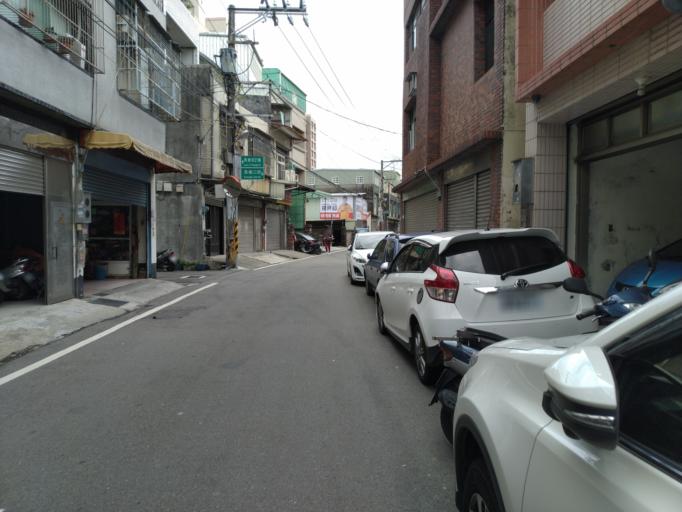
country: TW
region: Taiwan
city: Taoyuan City
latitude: 24.9784
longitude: 121.2495
